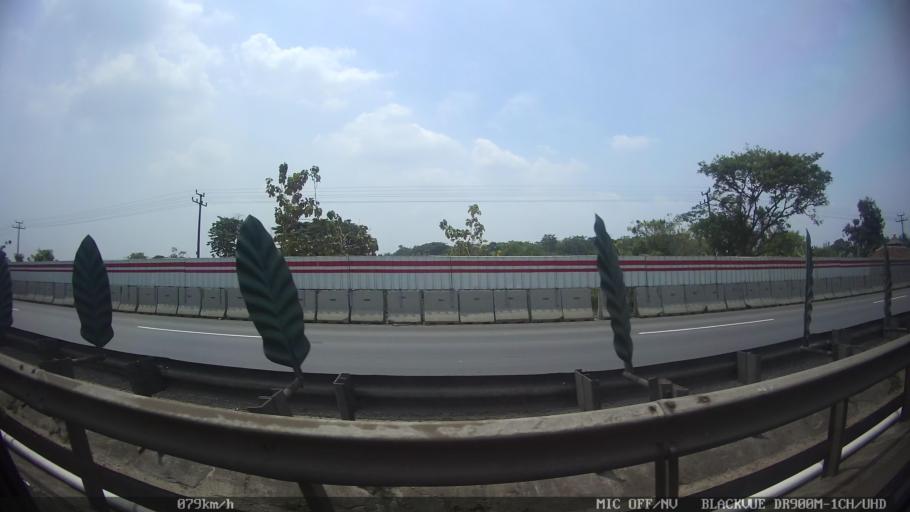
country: ID
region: West Java
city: Kresek
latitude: -6.1493
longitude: 106.3026
